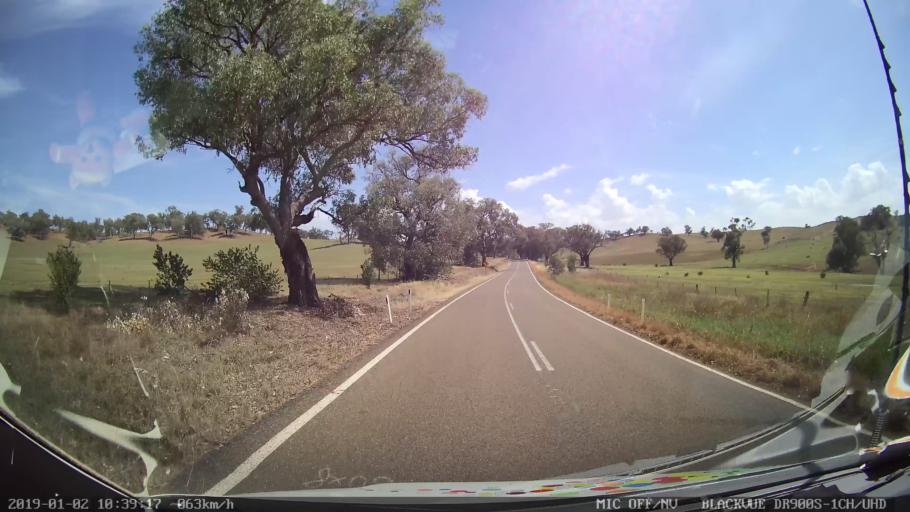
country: AU
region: New South Wales
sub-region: Gundagai
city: Gundagai
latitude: -34.8123
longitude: 148.3194
